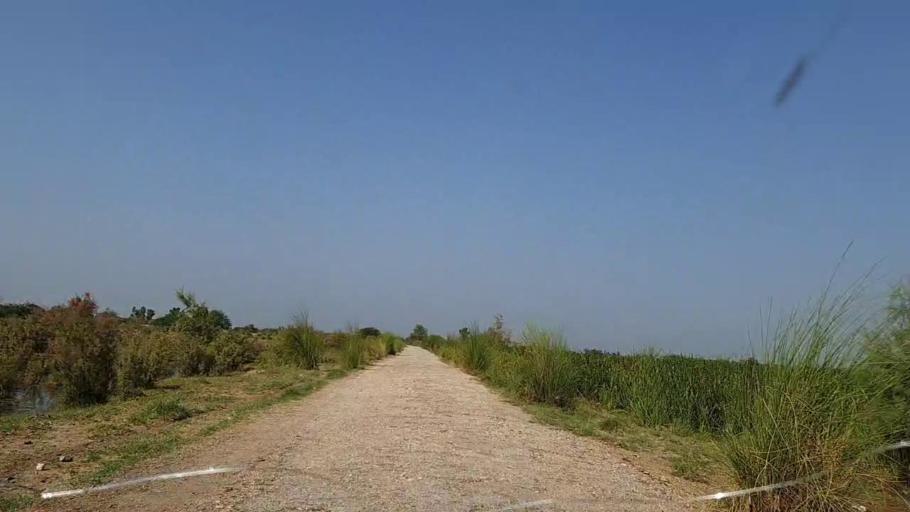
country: PK
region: Sindh
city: Khanpur
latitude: 27.7058
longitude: 69.3873
